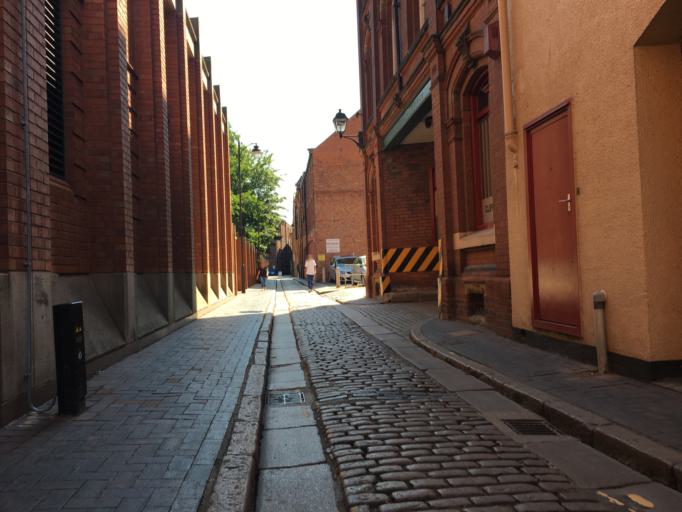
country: GB
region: England
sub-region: City of Kingston upon Hull
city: Hull
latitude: 53.7438
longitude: -0.3319
